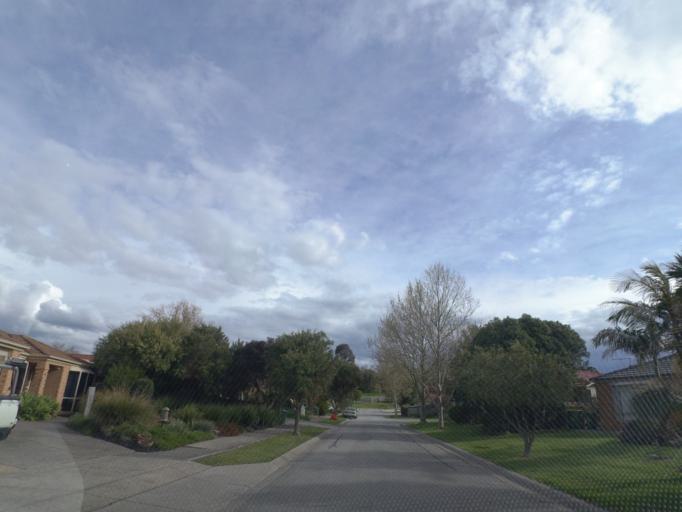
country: AU
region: Victoria
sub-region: Yarra Ranges
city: Lilydale
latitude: -37.7425
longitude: 145.3498
